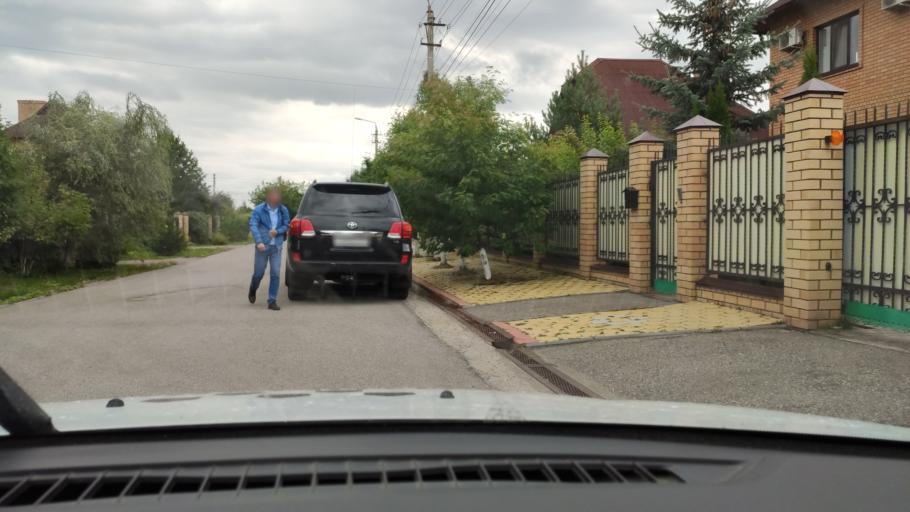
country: RU
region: Perm
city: Kondratovo
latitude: 57.9771
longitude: 56.1119
